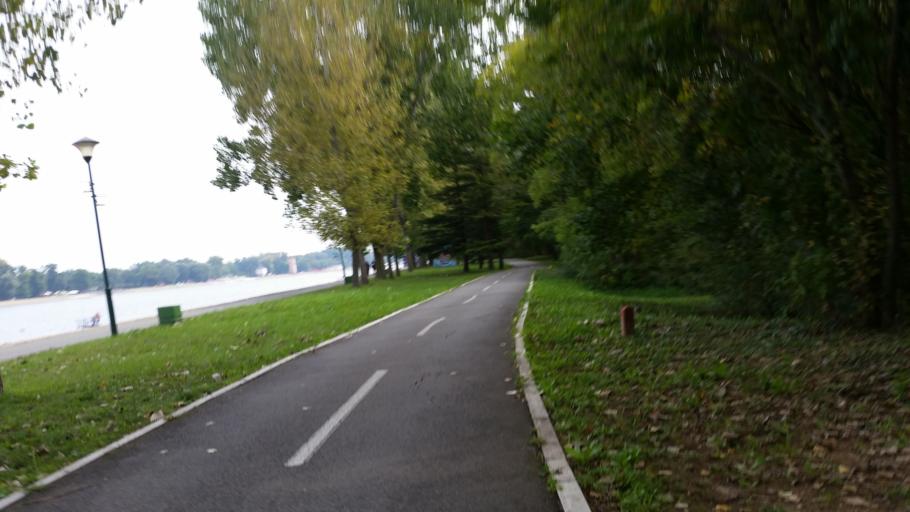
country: RS
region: Central Serbia
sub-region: Belgrade
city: Cukarica
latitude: 44.7805
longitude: 20.3847
